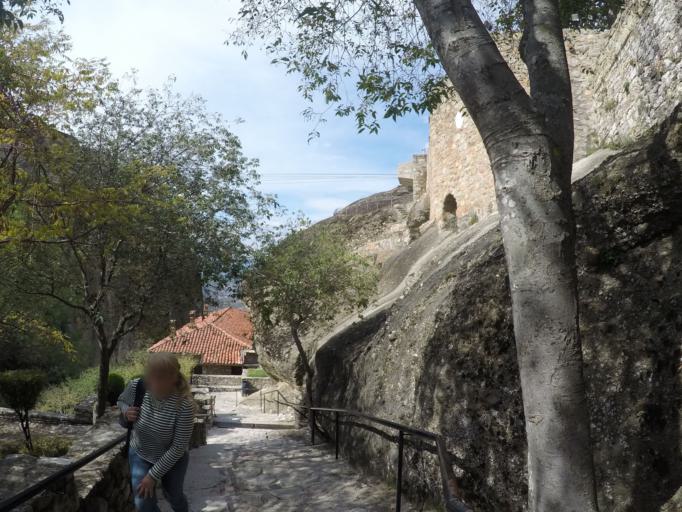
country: GR
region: Thessaly
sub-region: Trikala
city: Kastraki
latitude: 39.7267
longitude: 21.6273
